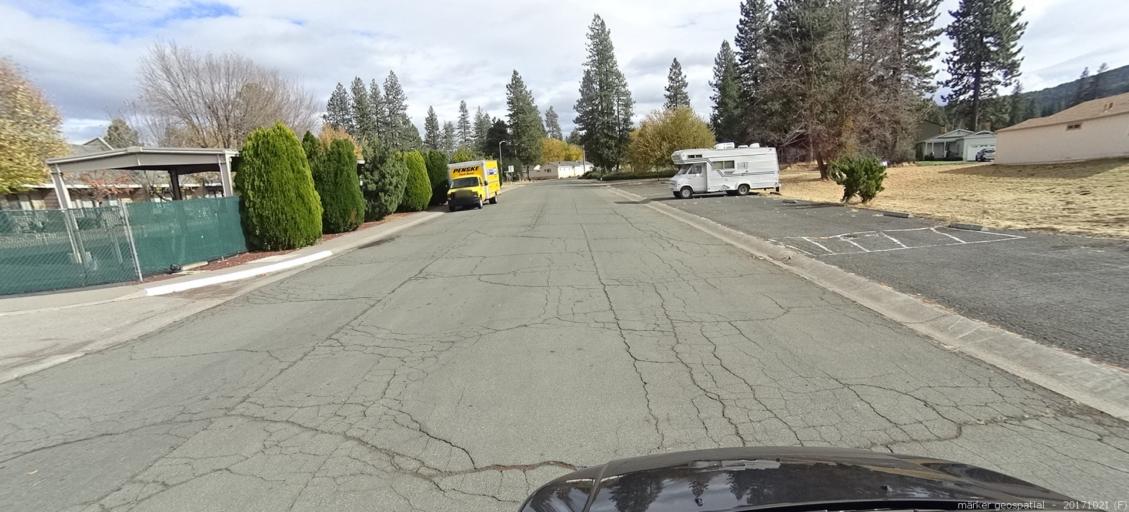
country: US
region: California
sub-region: Shasta County
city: Burney
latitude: 40.8880
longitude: -121.6583
